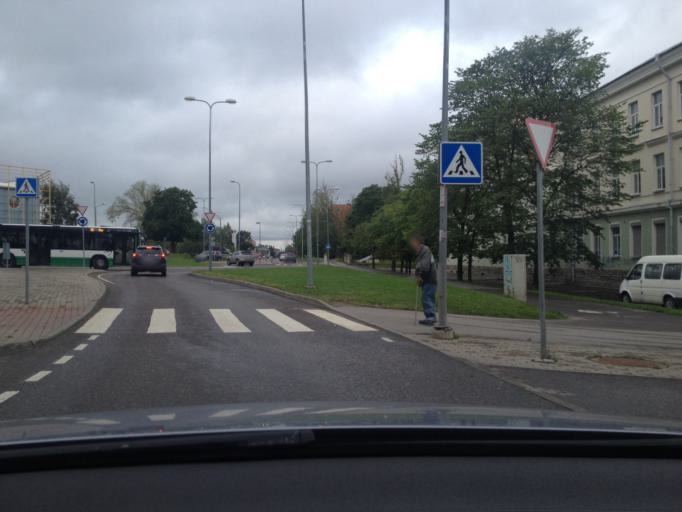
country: EE
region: Harju
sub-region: Tallinna linn
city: Tallinn
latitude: 59.4327
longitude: 24.8118
